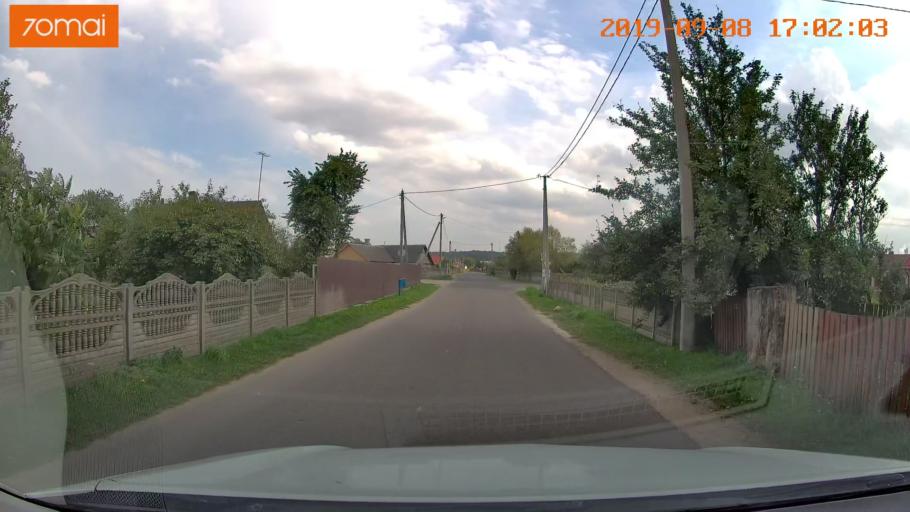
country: BY
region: Grodnenskaya
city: Hrodna
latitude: 53.7055
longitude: 23.9375
